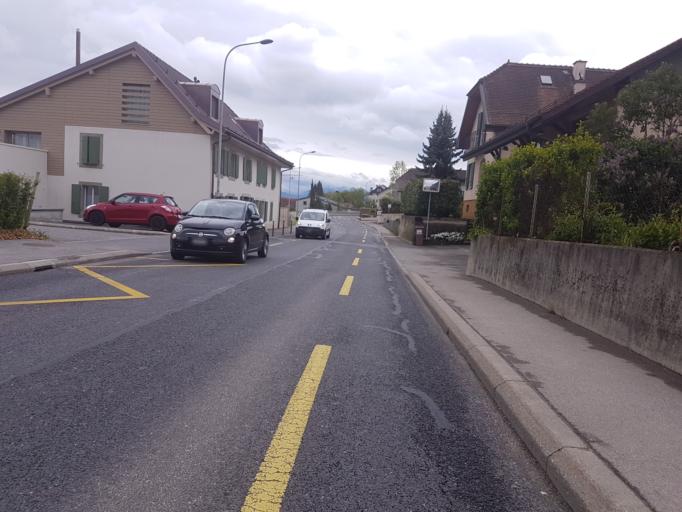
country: CH
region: Vaud
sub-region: Morges District
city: Preverenges
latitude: 46.5264
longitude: 6.5417
